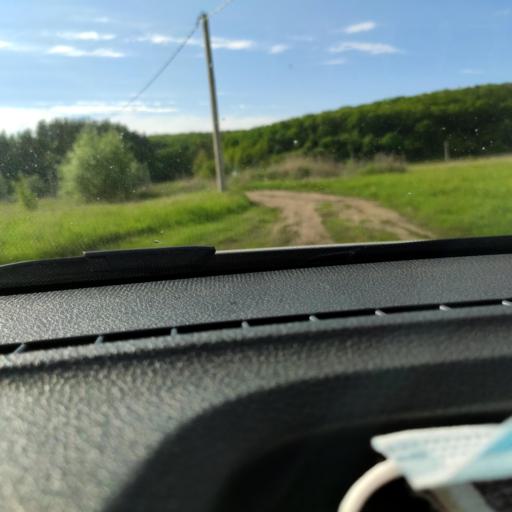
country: RU
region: Voronezj
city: Ramon'
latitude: 51.9379
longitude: 39.3740
